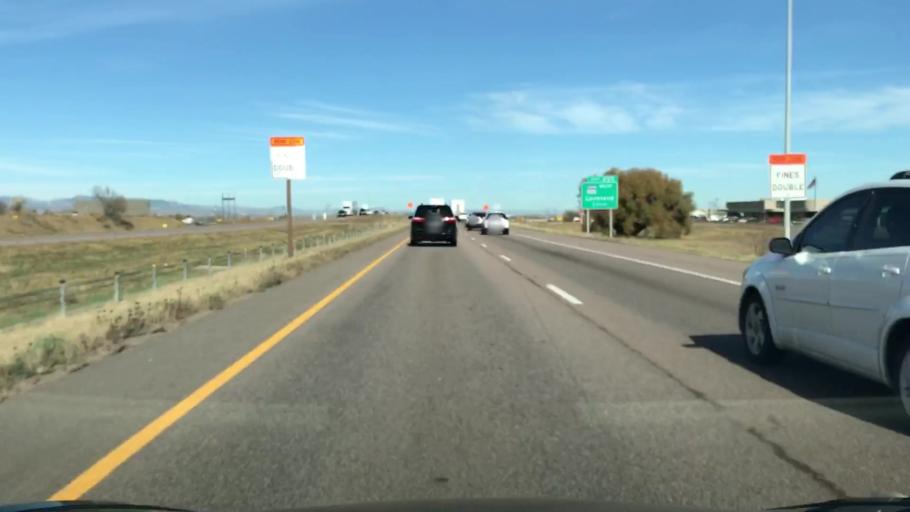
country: US
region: Colorado
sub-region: Weld County
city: Johnstown
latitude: 40.3605
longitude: -104.9842
